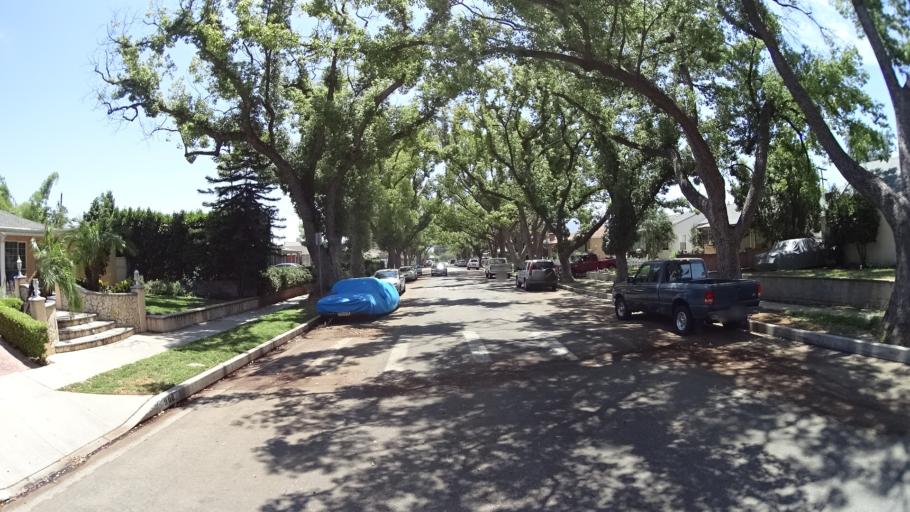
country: US
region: California
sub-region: Los Angeles County
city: Burbank
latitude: 34.1794
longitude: -118.3304
